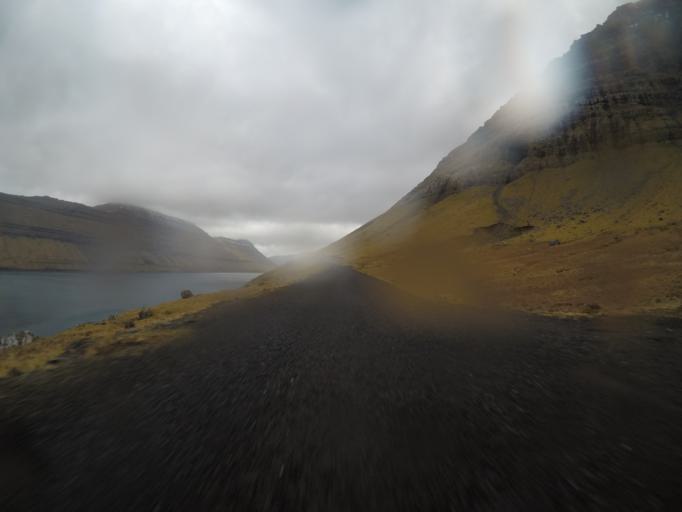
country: FO
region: Nordoyar
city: Klaksvik
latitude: 62.3326
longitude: -6.5748
